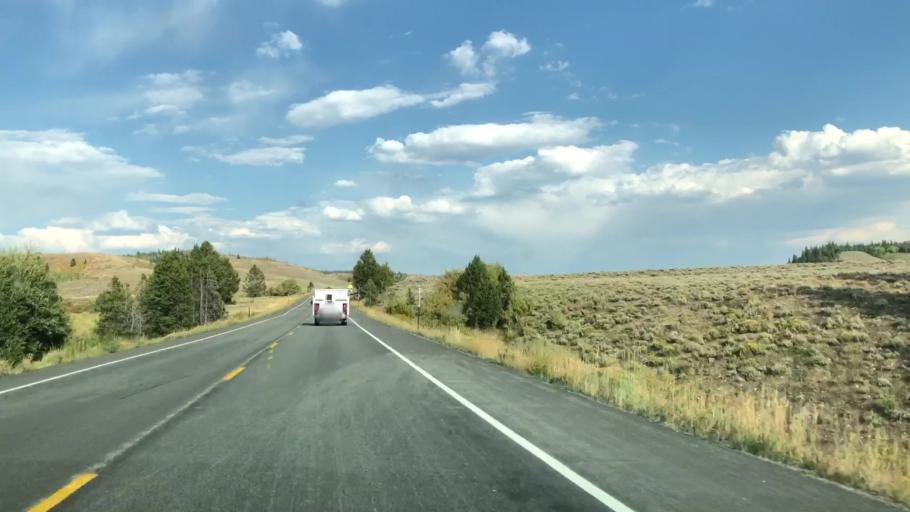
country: US
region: Wyoming
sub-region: Teton County
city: Hoback
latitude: 43.1559
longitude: -110.3090
